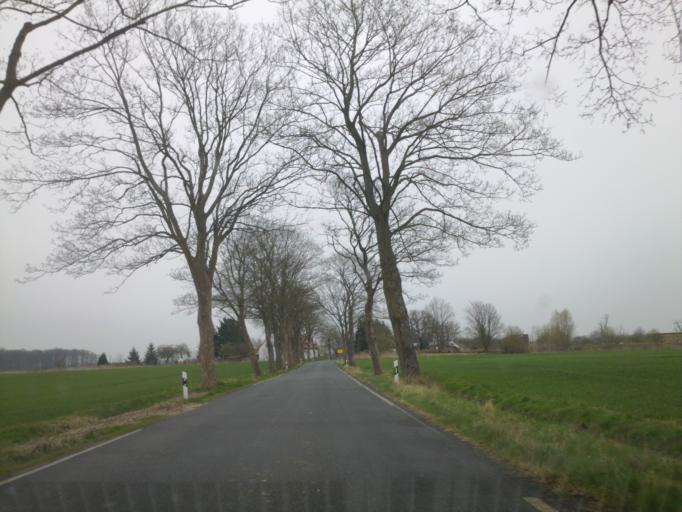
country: DE
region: Mecklenburg-Vorpommern
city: Velgast
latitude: 54.2202
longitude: 12.7345
